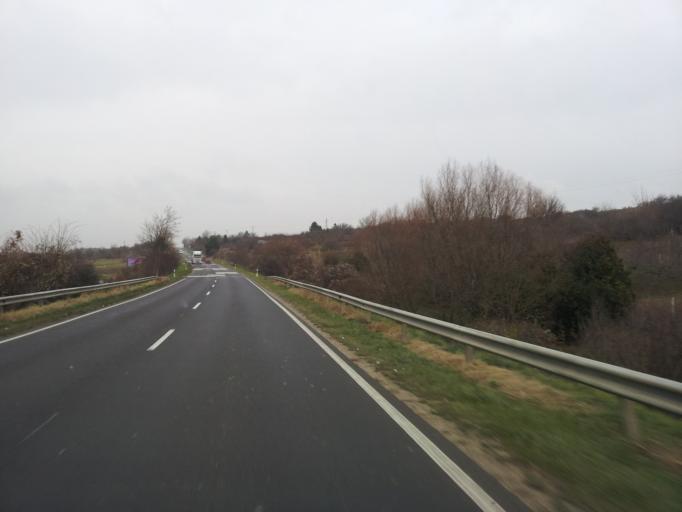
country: HU
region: Veszprem
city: Veszprem
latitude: 47.0971
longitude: 17.8742
